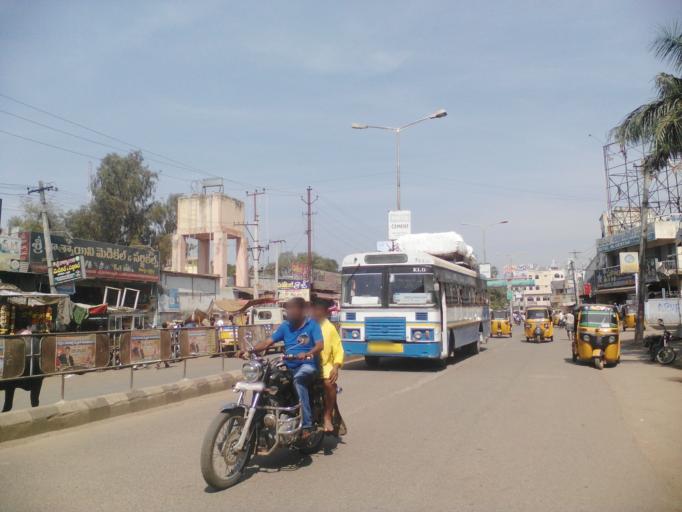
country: IN
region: Andhra Pradesh
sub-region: Kurnool
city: Nandyal
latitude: 15.4896
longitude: 78.4799
